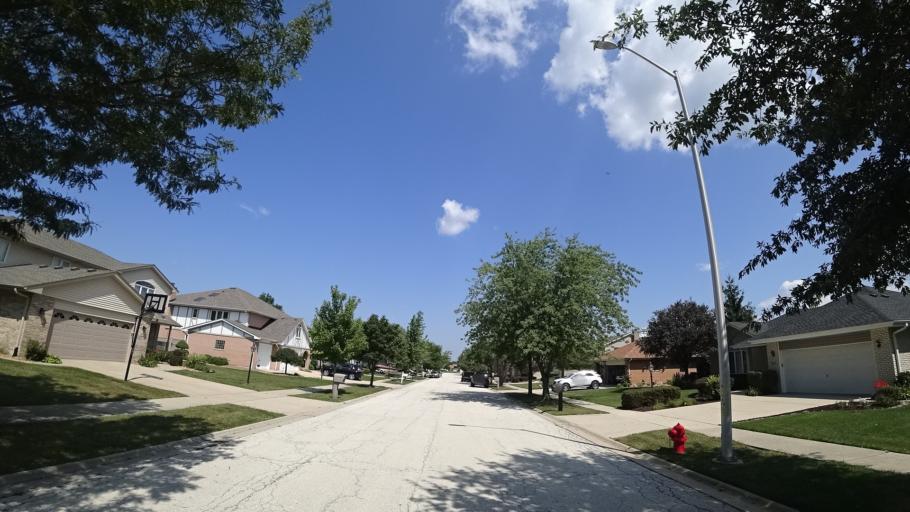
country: US
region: Illinois
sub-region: Cook County
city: Tinley Park
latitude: 41.6078
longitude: -87.7882
